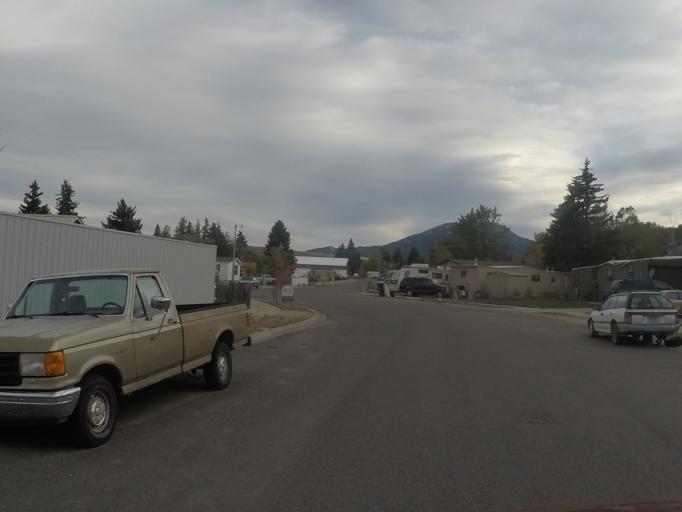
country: US
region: Montana
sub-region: Carbon County
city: Red Lodge
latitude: 45.1978
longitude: -109.2482
